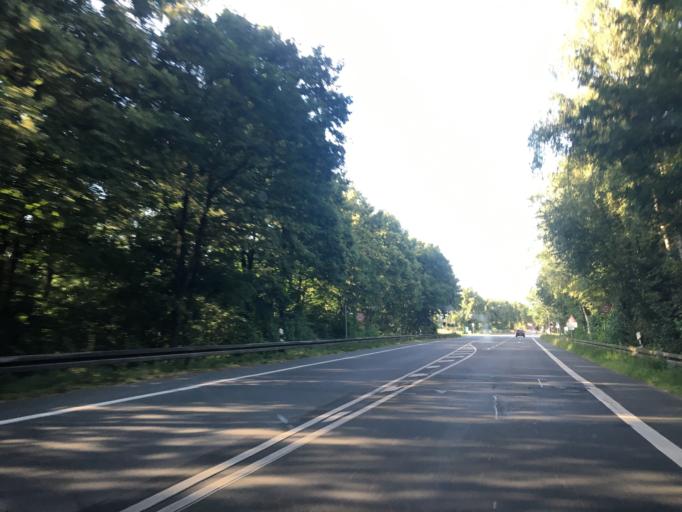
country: DE
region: North Rhine-Westphalia
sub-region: Regierungsbezirk Munster
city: Dulmen
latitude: 51.8036
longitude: 7.2396
